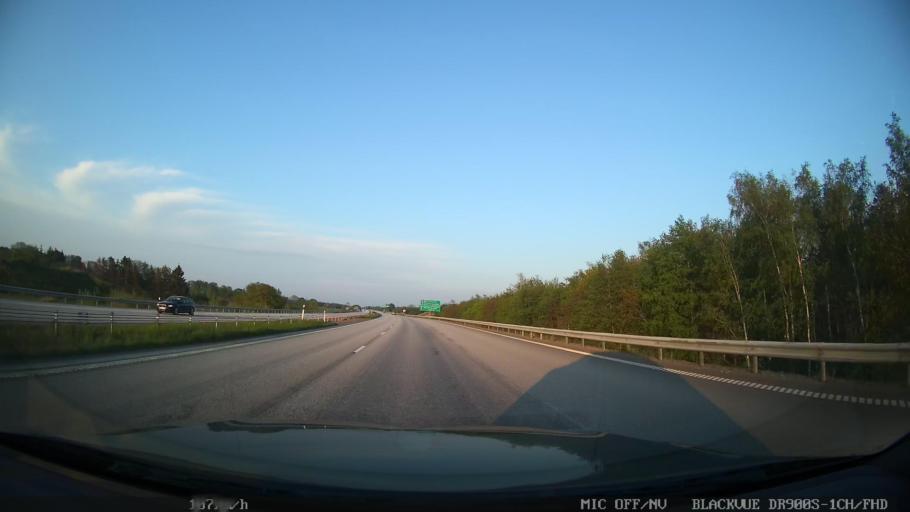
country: SE
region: Skane
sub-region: Helsingborg
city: Odakra
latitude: 56.0852
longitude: 12.7614
